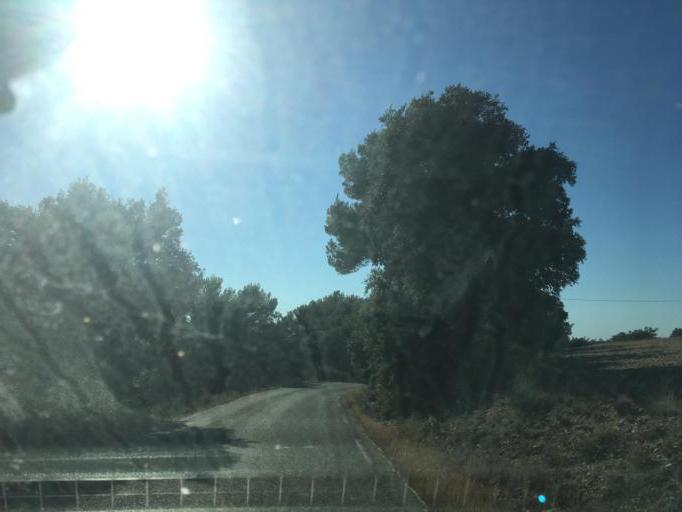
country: FR
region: Provence-Alpes-Cote d'Azur
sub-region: Departement du Var
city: Regusse
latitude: 43.7062
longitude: 6.1434
